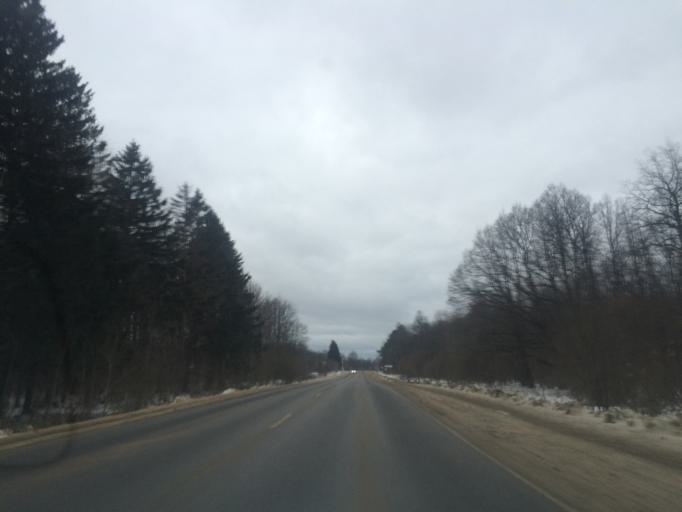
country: RU
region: Tula
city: Odoyev
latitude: 54.0070
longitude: 36.7857
